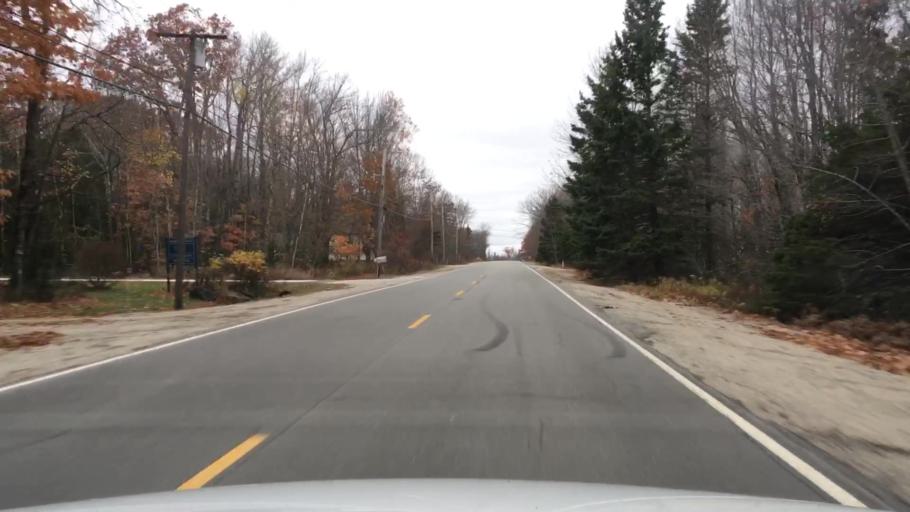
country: US
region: Maine
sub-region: Hancock County
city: Sedgwick
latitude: 44.3984
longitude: -68.5886
